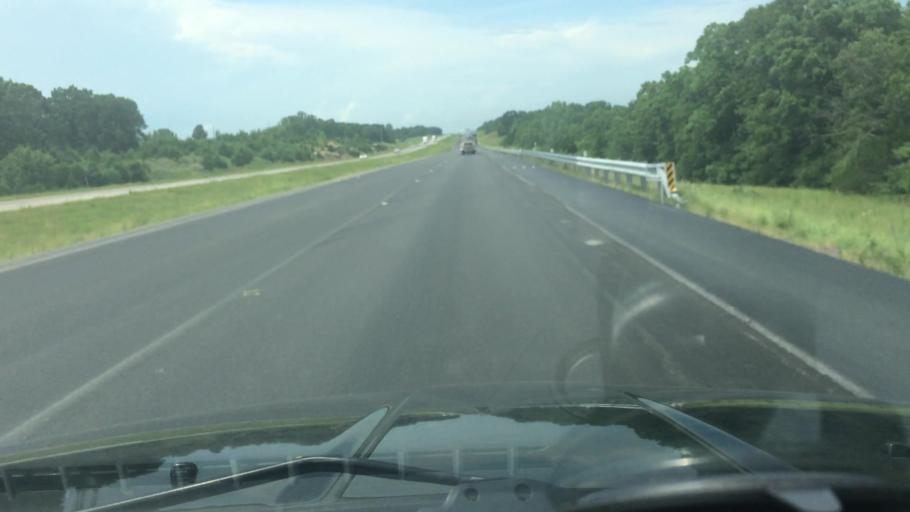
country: US
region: Missouri
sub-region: Saint Clair County
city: Osceola
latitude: 37.9557
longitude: -93.6419
